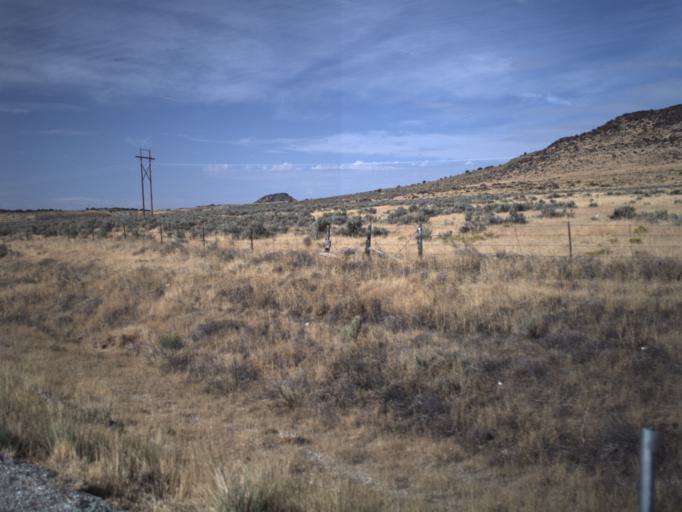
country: US
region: Idaho
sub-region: Minidoka County
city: Rupert
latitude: 41.8412
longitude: -113.1412
